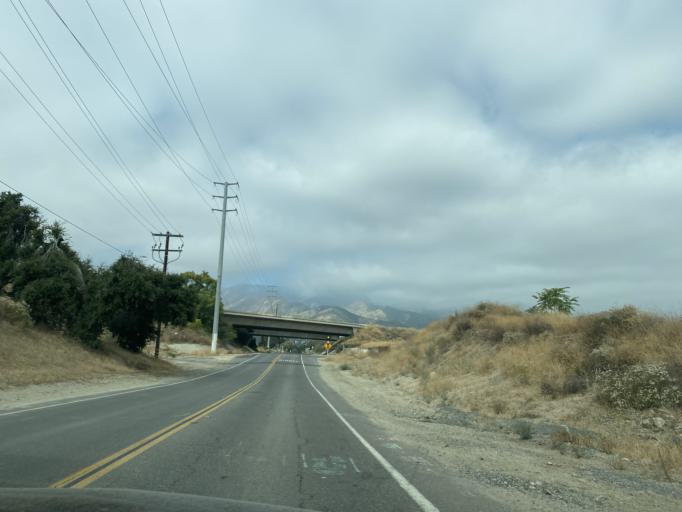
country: US
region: California
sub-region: Riverside County
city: El Cerrito
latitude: 33.7627
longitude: -117.4704
